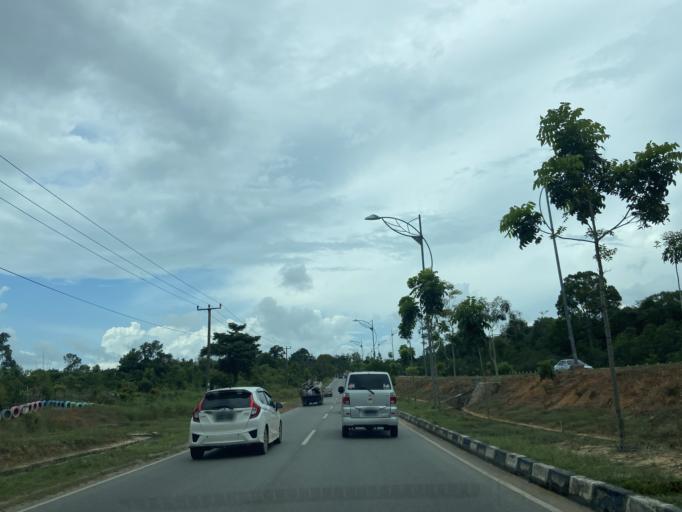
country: SG
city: Singapore
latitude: 1.1296
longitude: 104.1086
